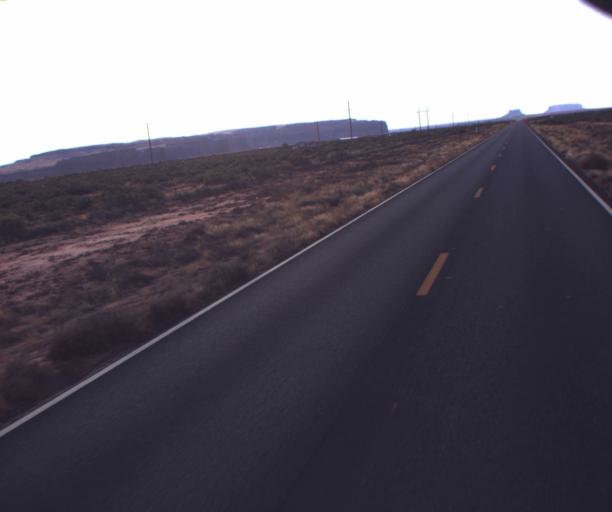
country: US
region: Arizona
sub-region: Apache County
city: Many Farms
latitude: 36.6649
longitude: -109.5972
